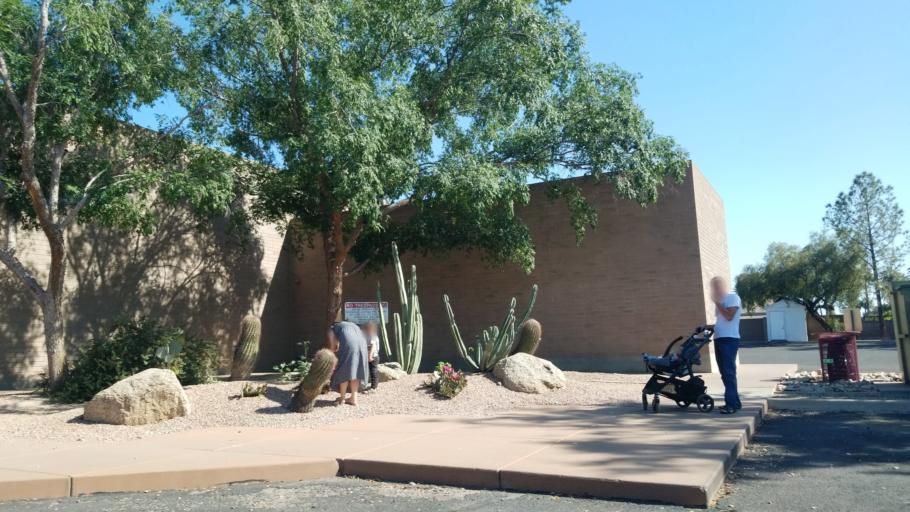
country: US
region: Arizona
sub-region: Maricopa County
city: Glendale
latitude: 33.5775
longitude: -112.1879
